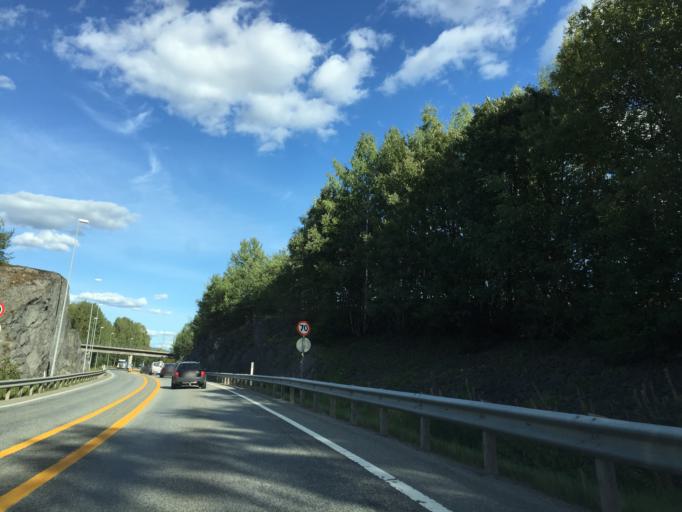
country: NO
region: Buskerud
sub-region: Nedre Eiker
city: Mjondalen
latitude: 59.7546
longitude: 9.9800
